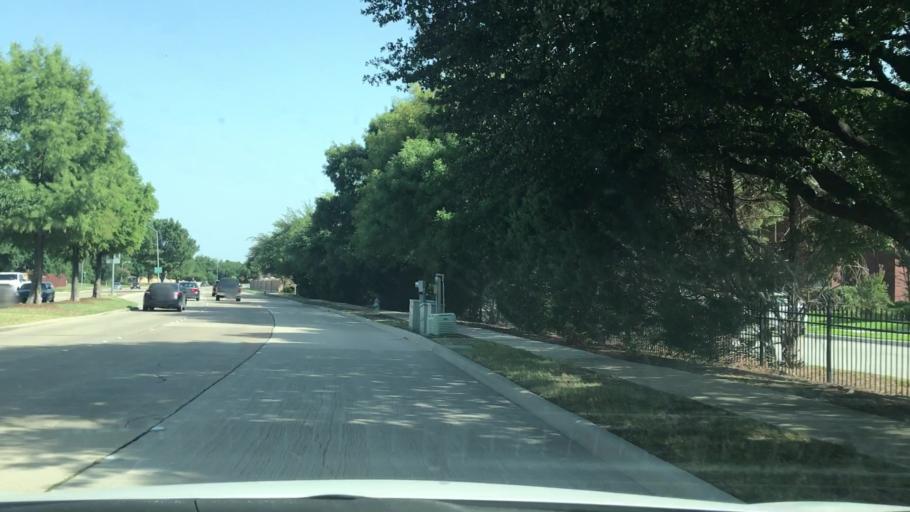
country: US
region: Texas
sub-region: Collin County
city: Allen
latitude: 33.0980
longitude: -96.7501
